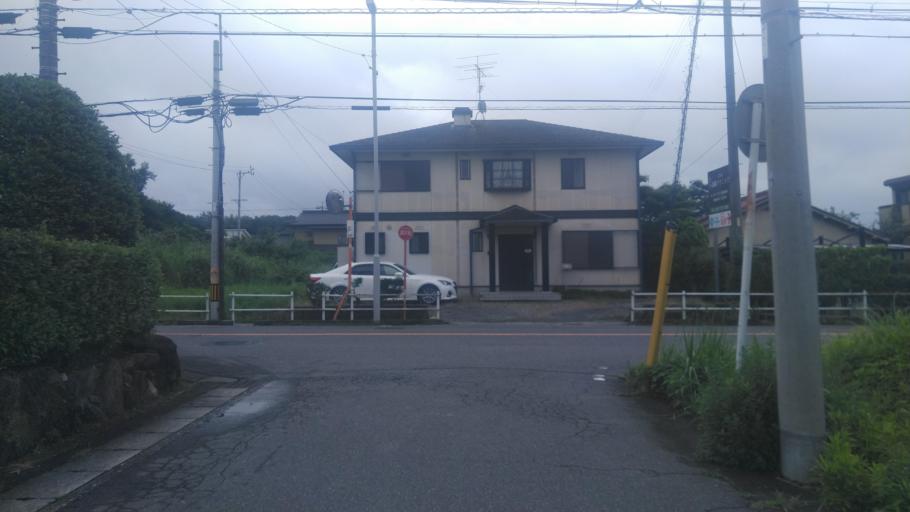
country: JP
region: Aichi
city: Kasugai
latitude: 35.2458
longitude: 137.0272
